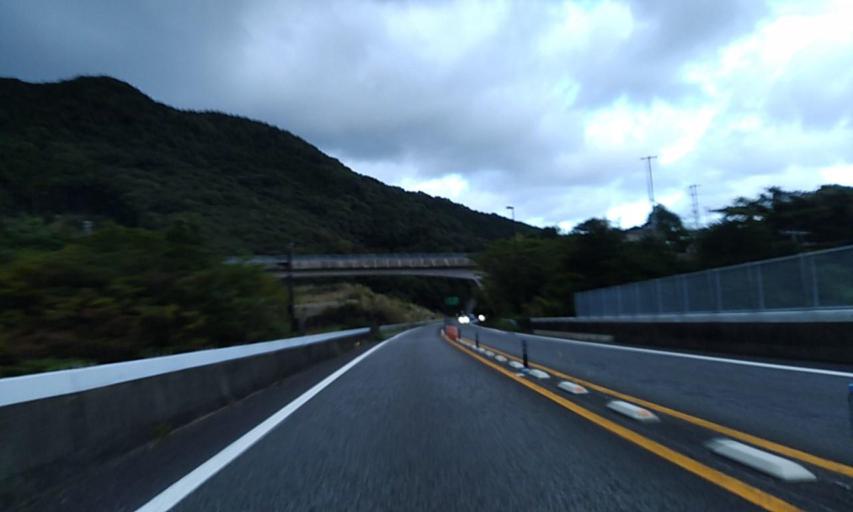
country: JP
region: Wakayama
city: Shingu
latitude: 33.6861
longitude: 135.9547
